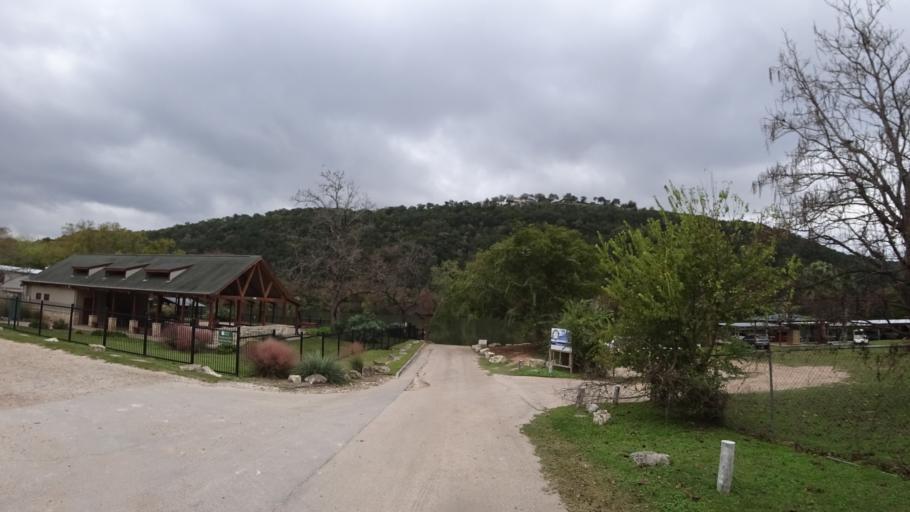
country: US
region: Texas
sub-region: Travis County
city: Bee Cave
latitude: 30.3276
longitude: -97.9181
